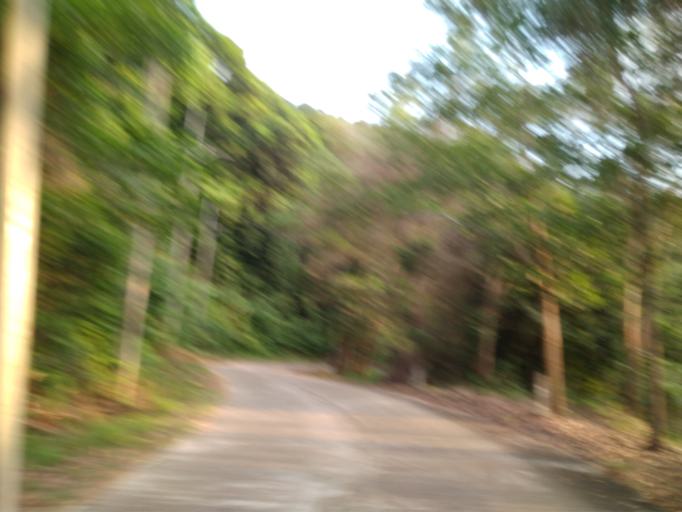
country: TH
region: Phangnga
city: Ko Yao
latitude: 8.1535
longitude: 98.6007
